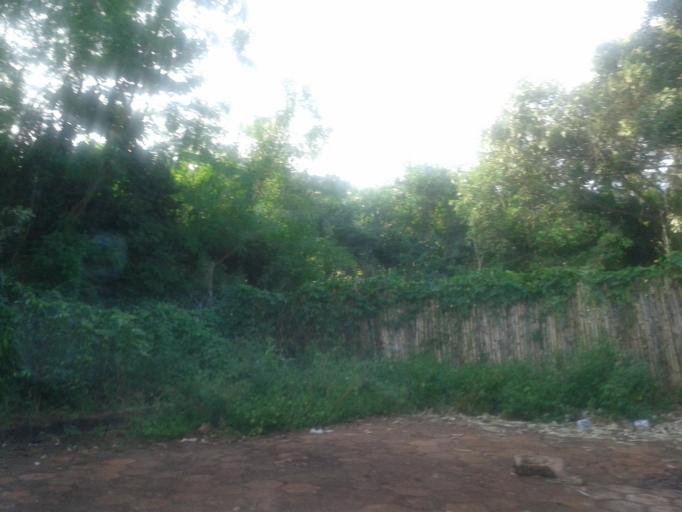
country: BR
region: Minas Gerais
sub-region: Capinopolis
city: Capinopolis
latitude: -18.6758
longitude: -49.5678
